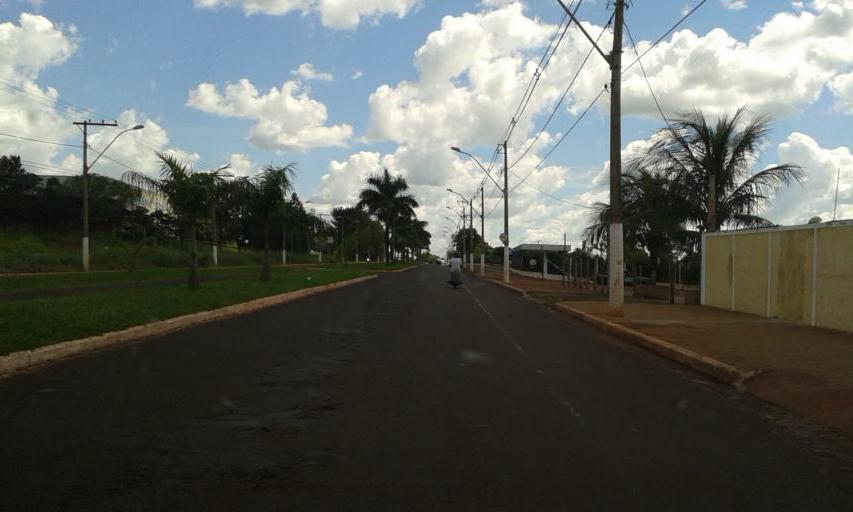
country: BR
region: Minas Gerais
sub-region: Ituiutaba
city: Ituiutaba
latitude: -18.9717
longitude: -49.4794
